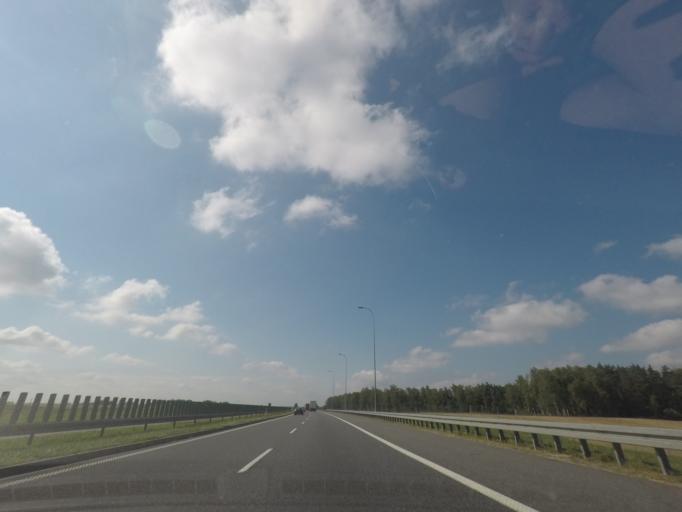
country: PL
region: Pomeranian Voivodeship
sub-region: Powiat starogardzki
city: Bobowo
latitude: 53.8821
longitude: 18.6270
